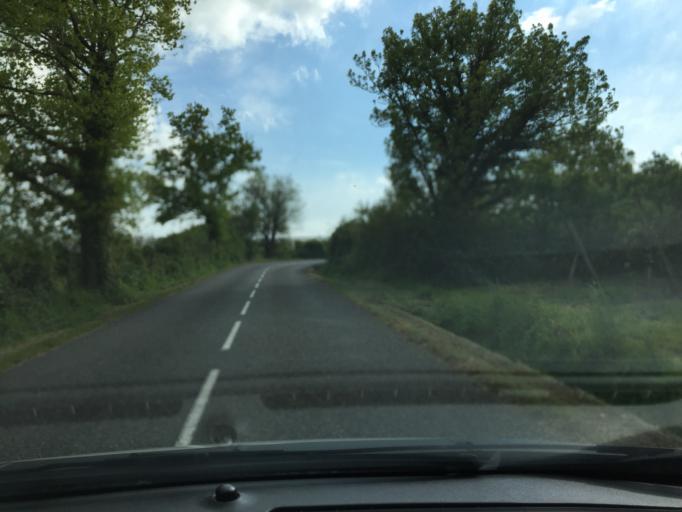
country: FR
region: Rhone-Alpes
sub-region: Departement du Rhone
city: Orlienas
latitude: 45.6483
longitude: 4.7011
